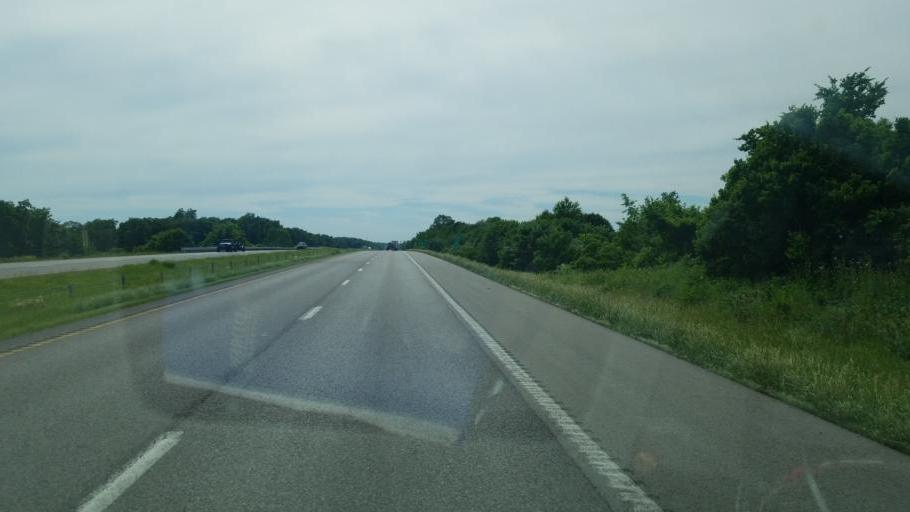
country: US
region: Missouri
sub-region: Saline County
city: Marshall
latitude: 38.9538
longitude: -93.0957
